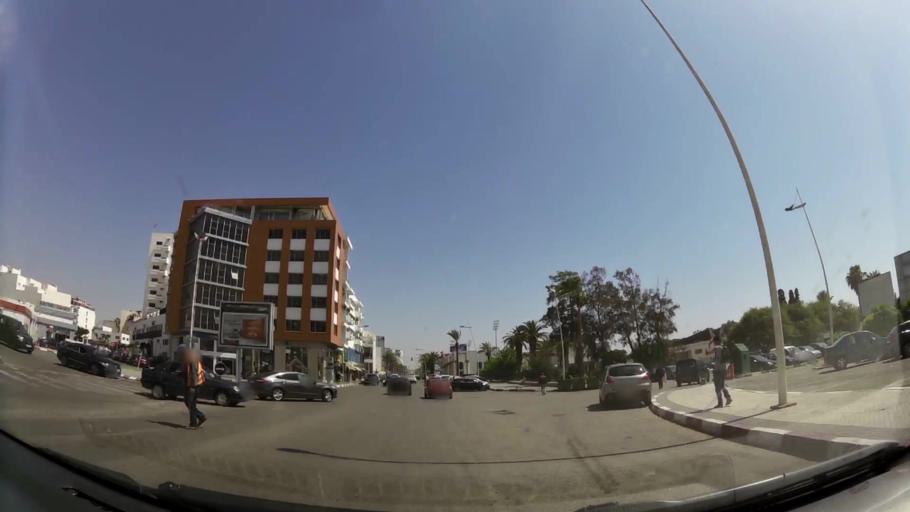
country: MA
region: Souss-Massa-Draa
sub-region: Agadir-Ida-ou-Tnan
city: Agadir
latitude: 30.4182
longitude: -9.5972
